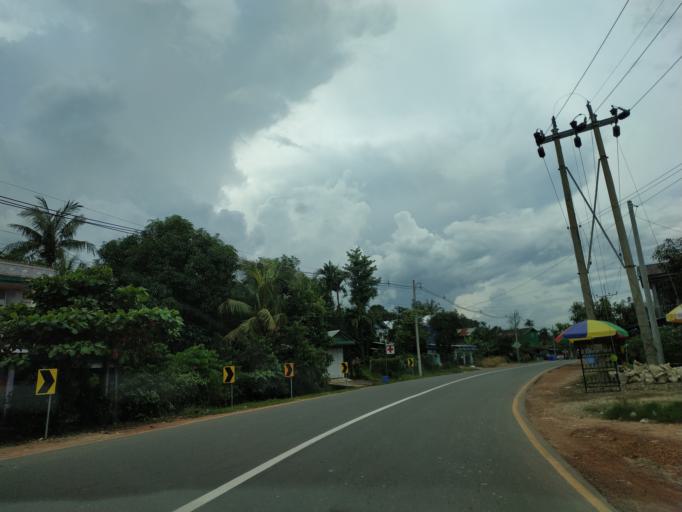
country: MM
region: Tanintharyi
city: Dawei
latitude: 14.0693
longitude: 98.2209
